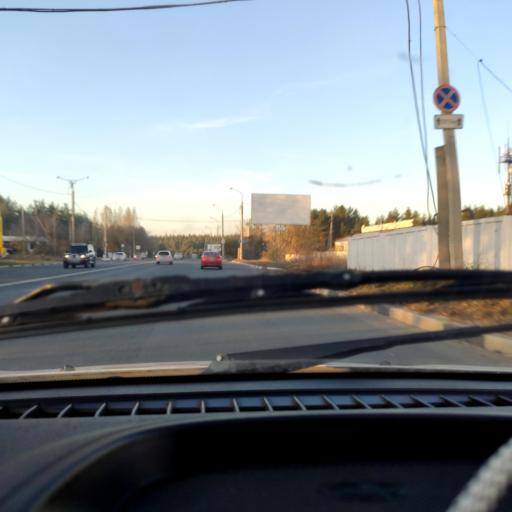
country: RU
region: Samara
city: Zhigulevsk
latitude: 53.4974
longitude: 49.4732
